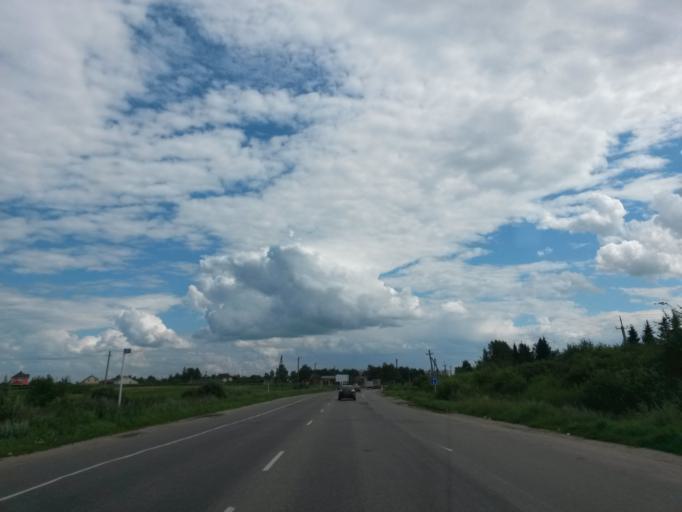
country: RU
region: Ivanovo
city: Novo-Talitsy
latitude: 57.0115
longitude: 40.8323
